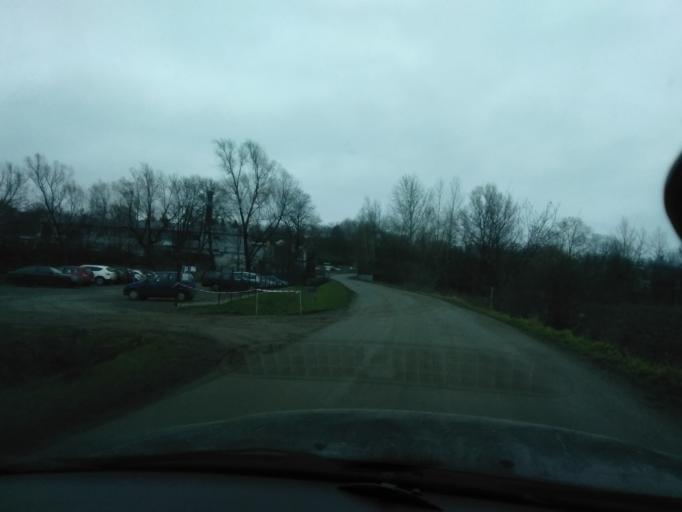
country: PL
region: Subcarpathian Voivodeship
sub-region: Powiat przeworski
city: Zarzecze
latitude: 49.9372
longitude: 22.5676
